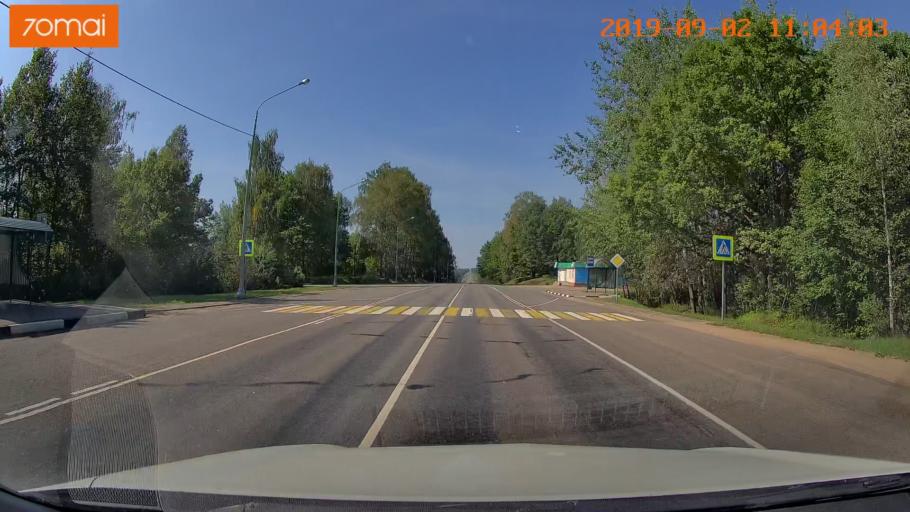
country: RU
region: Smolensk
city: Yekimovichi
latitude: 54.1287
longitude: 33.3412
